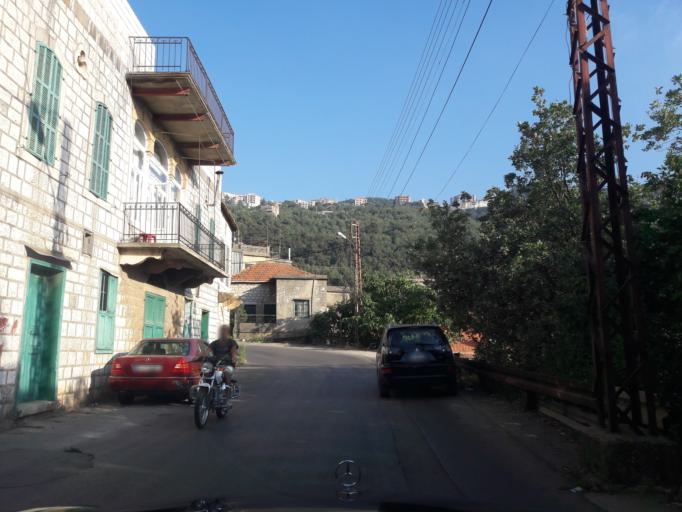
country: LB
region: Mont-Liban
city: Djounie
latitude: 33.9259
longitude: 35.6726
